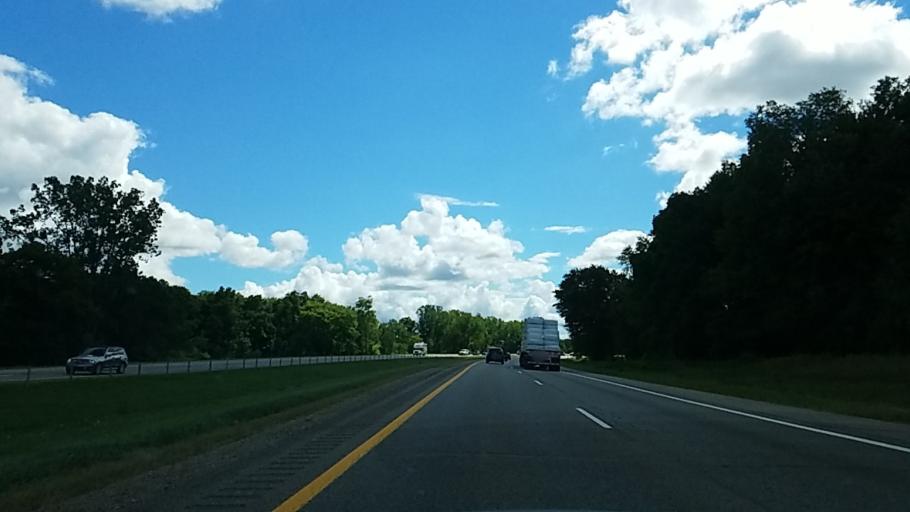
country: US
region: Michigan
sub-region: Livingston County
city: Brighton
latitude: 42.5646
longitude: -83.7406
